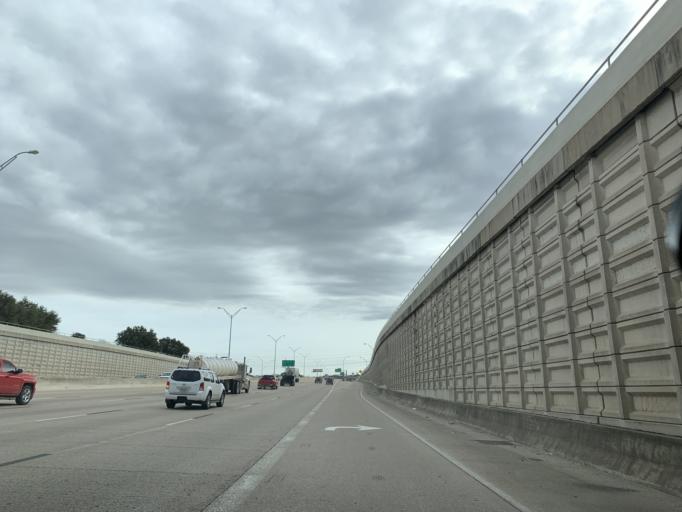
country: US
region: Texas
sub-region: Tarrant County
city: Edgecliff Village
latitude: 32.6780
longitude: -97.3873
